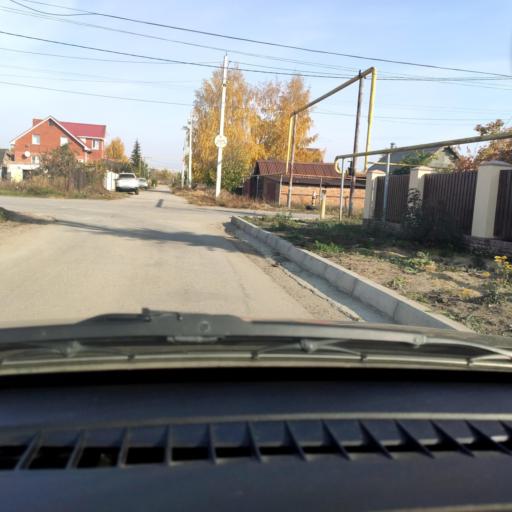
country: RU
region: Samara
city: Podstepki
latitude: 53.5129
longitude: 49.2370
